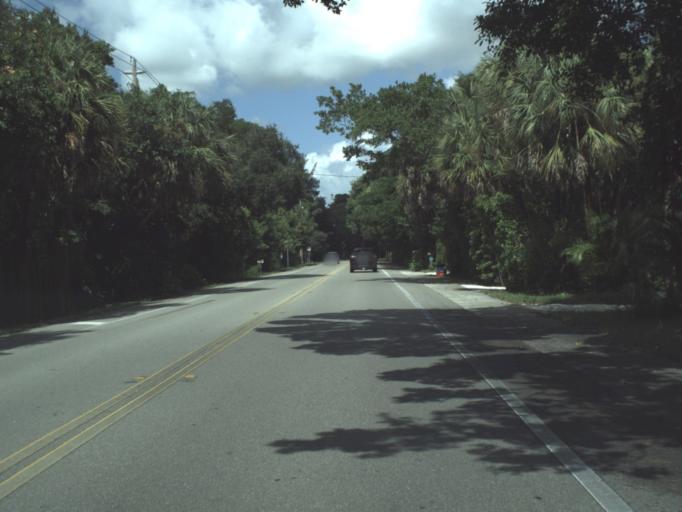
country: US
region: Florida
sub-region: Sarasota County
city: Siesta Key
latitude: 27.2881
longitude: -82.5576
